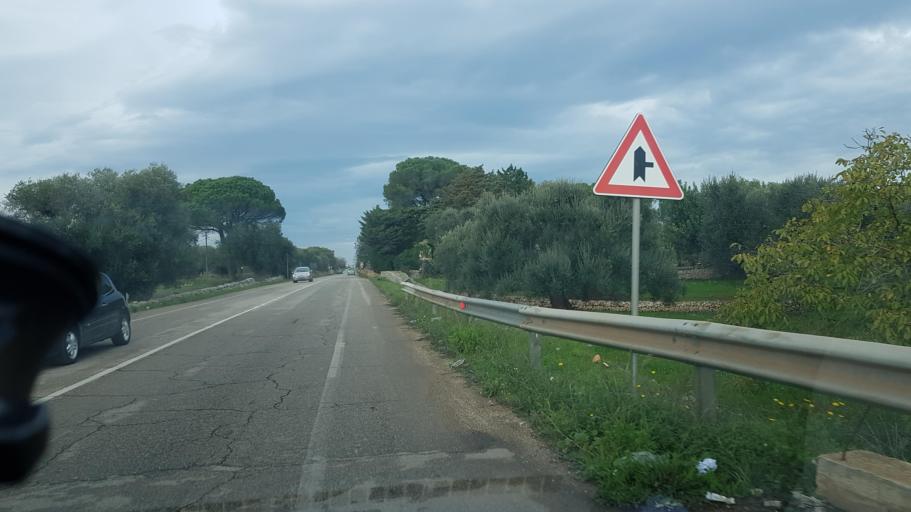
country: IT
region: Apulia
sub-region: Provincia di Brindisi
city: San Vito dei Normanni
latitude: 40.6699
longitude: 17.6948
